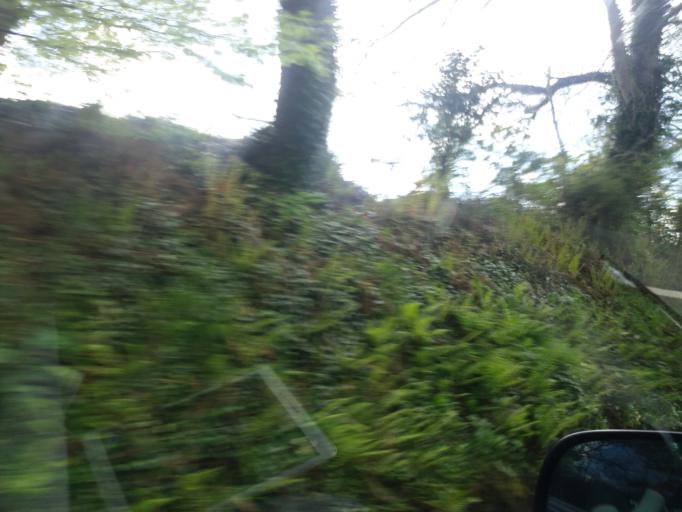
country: IE
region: Munster
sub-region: Waterford
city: Waterford
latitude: 52.2345
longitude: -7.0310
